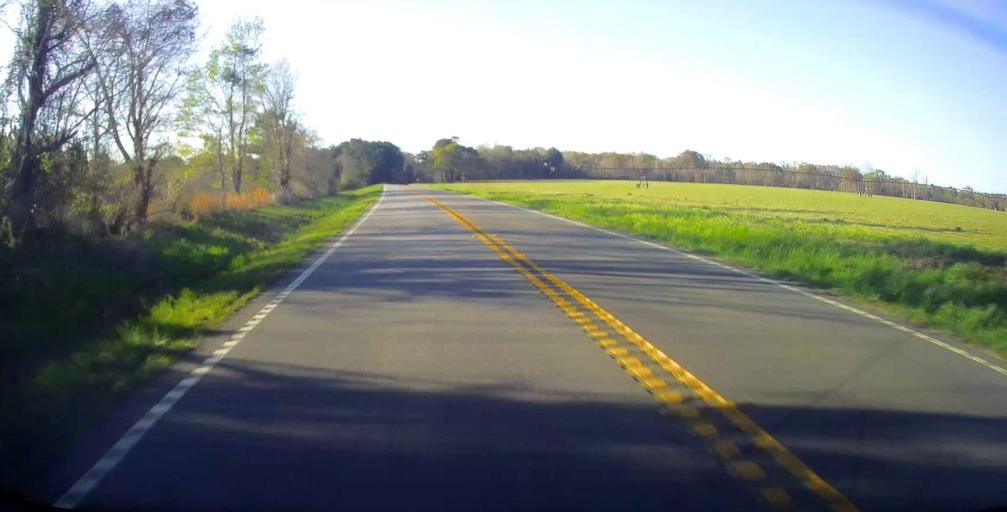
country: US
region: Georgia
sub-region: Pulaski County
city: Hawkinsville
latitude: 32.1881
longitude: -83.3665
